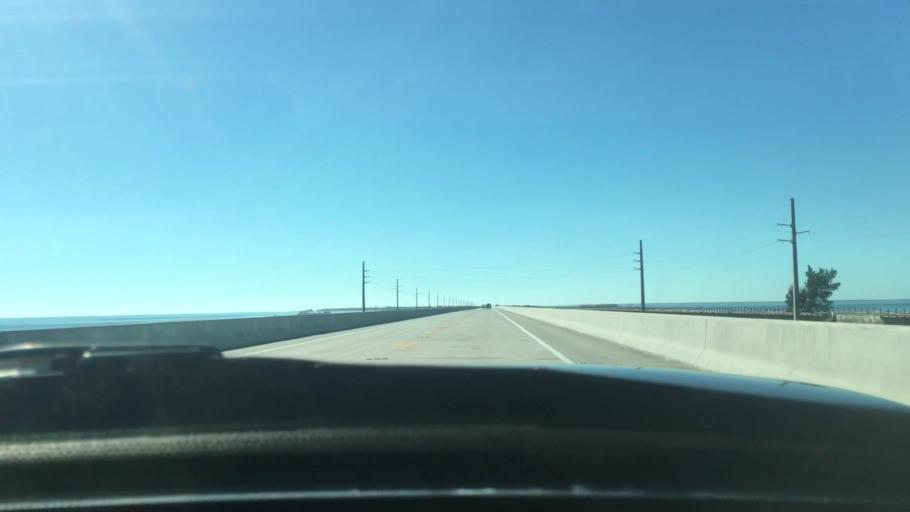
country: US
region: Florida
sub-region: Monroe County
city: Marathon
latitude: 24.6896
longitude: -81.2029
